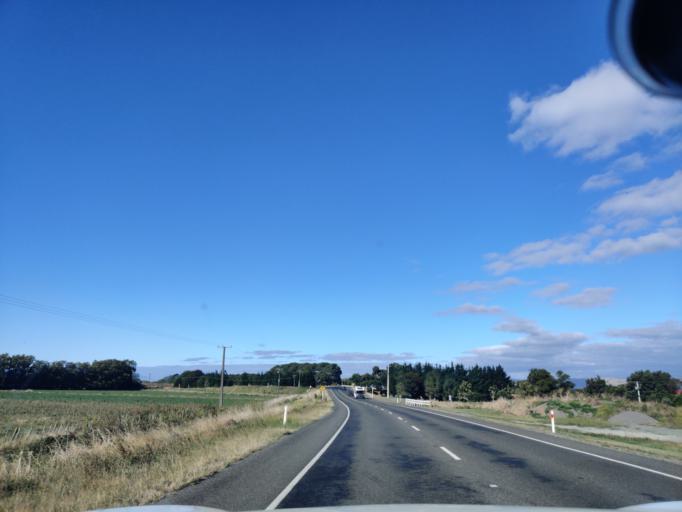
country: NZ
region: Manawatu-Wanganui
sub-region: Horowhenua District
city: Foxton
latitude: -40.4228
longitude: 175.4419
